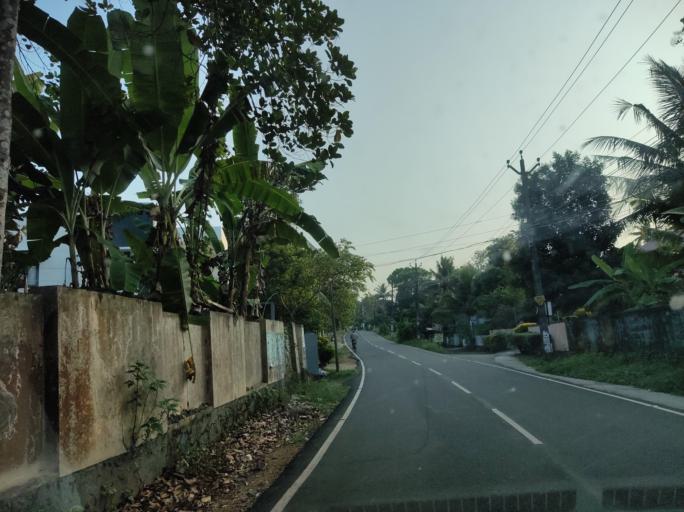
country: IN
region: Kerala
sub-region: Pattanamtitta
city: Tiruvalla
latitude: 9.3679
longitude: 76.5650
